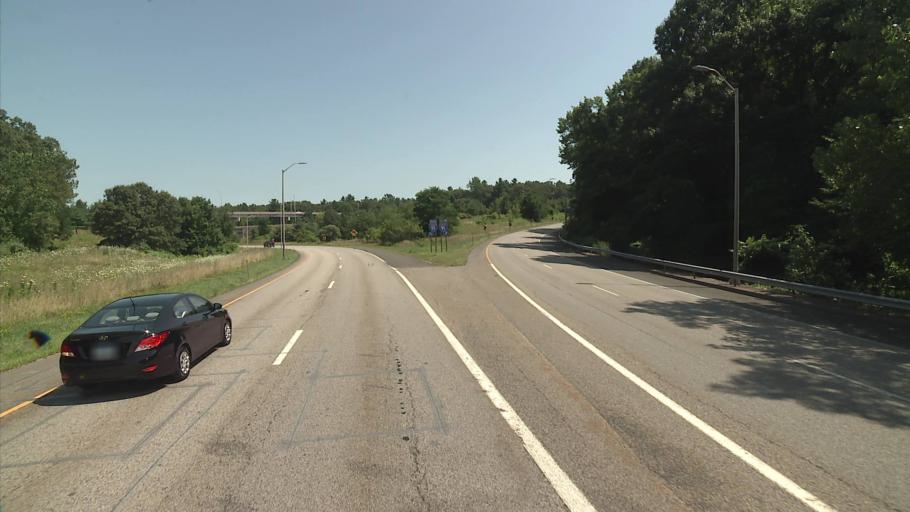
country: US
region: Connecticut
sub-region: Hartford County
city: Windsor Locks
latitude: 41.8999
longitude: -72.6420
